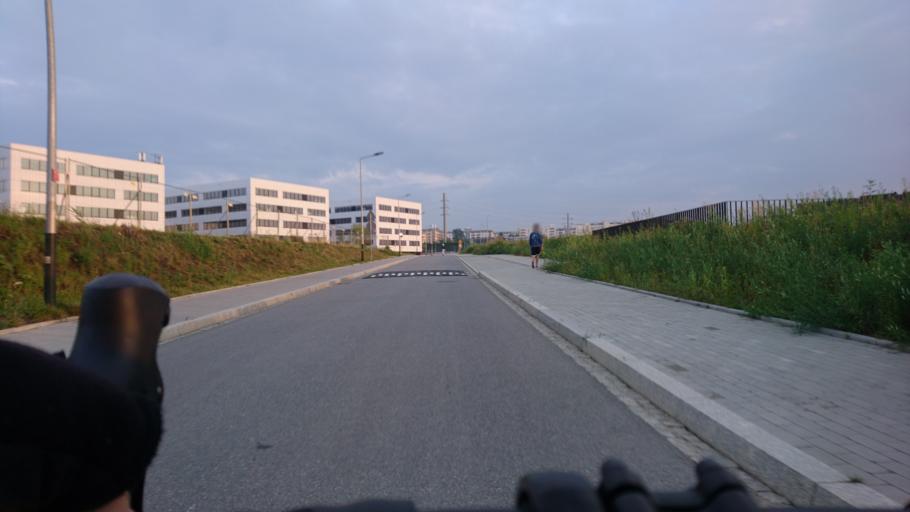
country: PL
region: Lesser Poland Voivodeship
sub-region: Krakow
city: Sidzina
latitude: 50.0209
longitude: 19.8887
